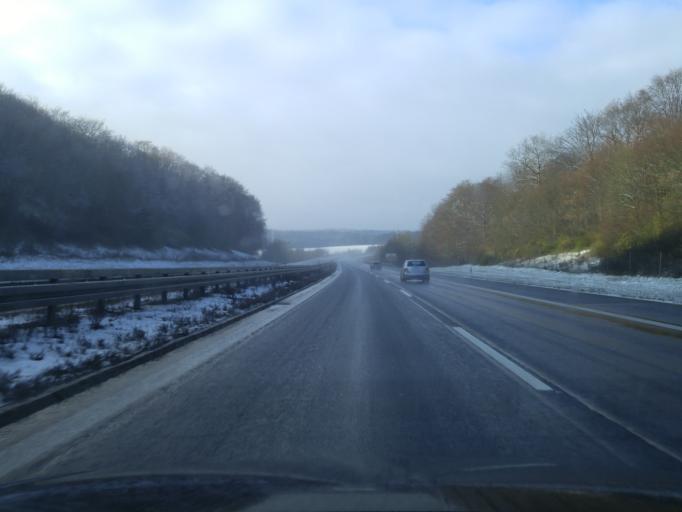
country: DE
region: Bavaria
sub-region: Regierungsbezirk Unterfranken
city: Wasserlosen
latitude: 50.0802
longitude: 10.0021
